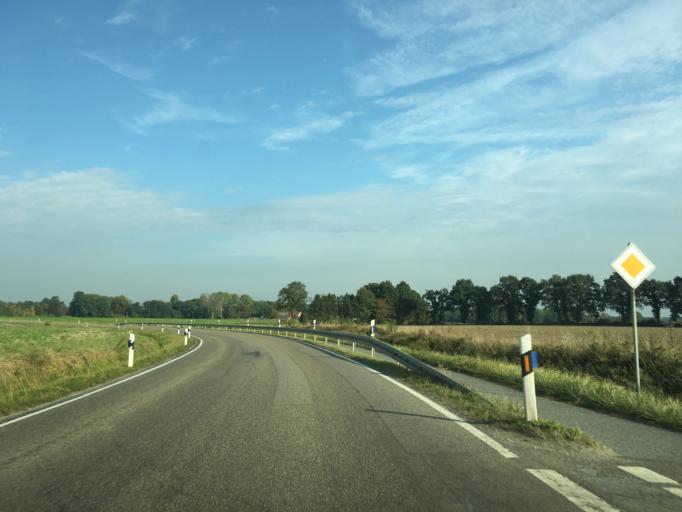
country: DE
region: North Rhine-Westphalia
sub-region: Regierungsbezirk Munster
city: Altenberge
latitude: 52.0592
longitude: 7.4858
